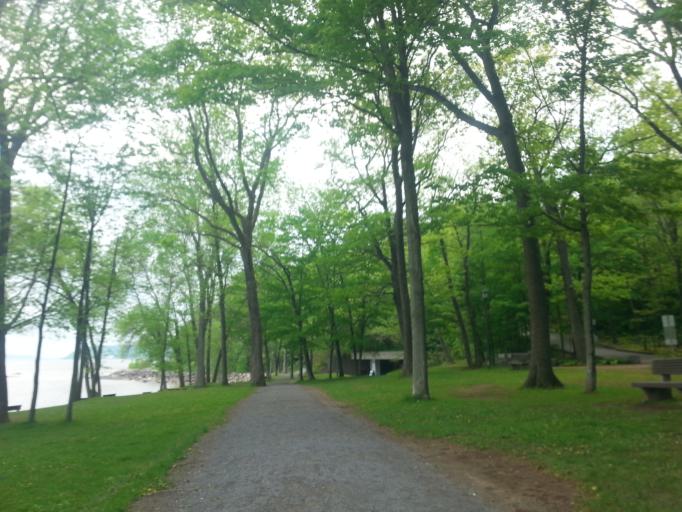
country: CA
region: Quebec
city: L'Ancienne-Lorette
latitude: 46.7505
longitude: -71.3140
